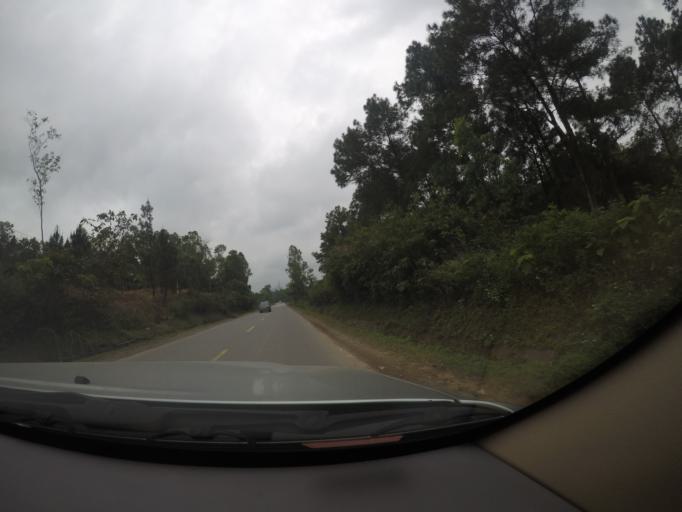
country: VN
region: Quang Binh
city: Quan Hau
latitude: 17.3490
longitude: 106.6244
